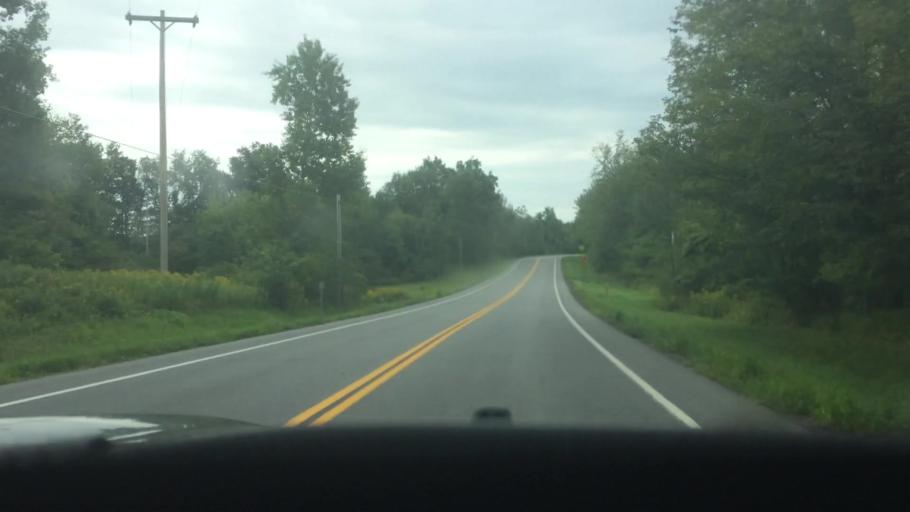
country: US
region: New York
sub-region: St. Lawrence County
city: Canton
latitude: 44.5240
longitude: -75.3365
